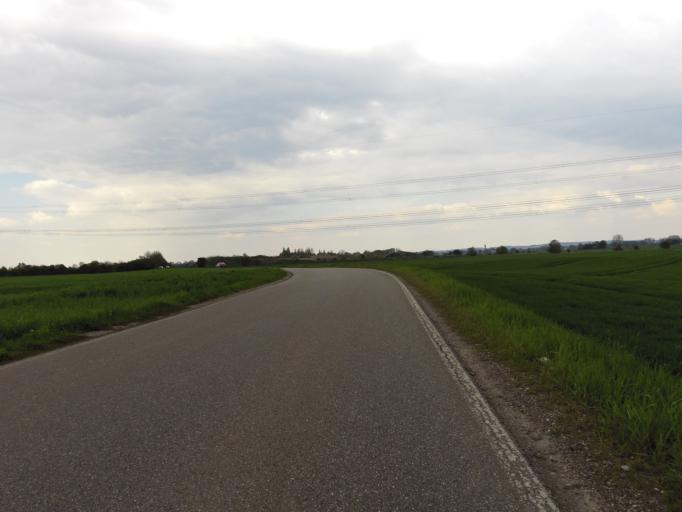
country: DE
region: Bavaria
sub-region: Upper Bavaria
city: Eitting
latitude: 48.3719
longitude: 11.9017
